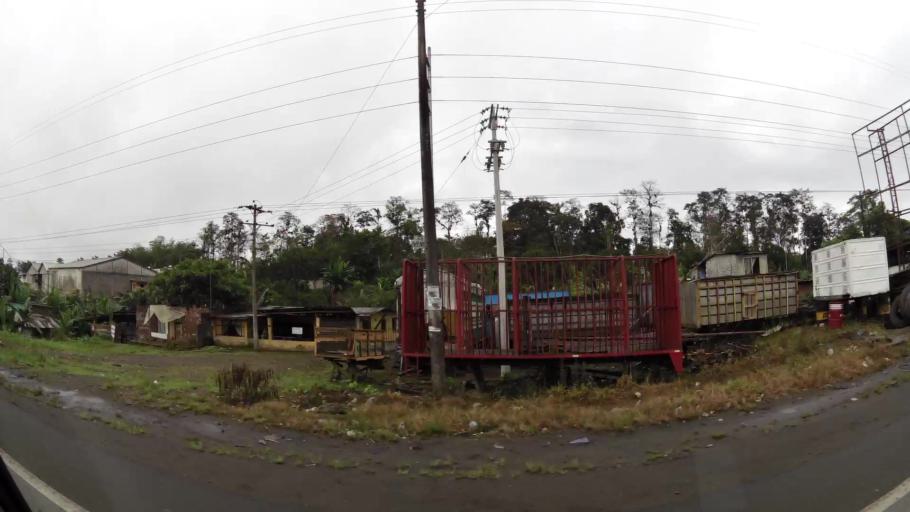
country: EC
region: Santo Domingo de los Tsachilas
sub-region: Canton Santo Domingo de los Colorados
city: Santo Domingo de los Colorados
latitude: -0.2688
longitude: -79.2011
